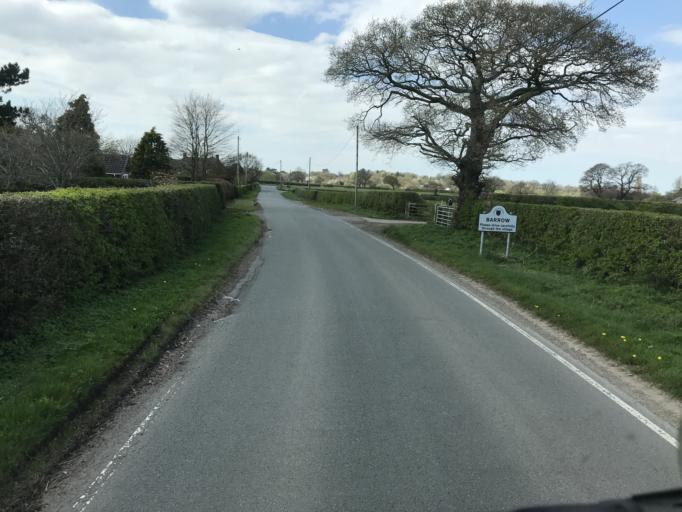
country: GB
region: England
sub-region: Cheshire West and Chester
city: Tarvin
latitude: 53.2113
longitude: -2.7710
